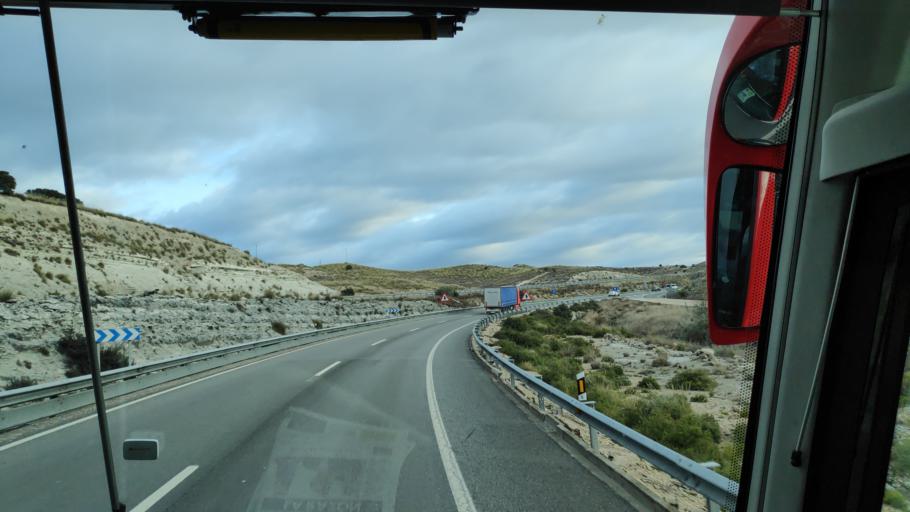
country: ES
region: Madrid
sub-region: Provincia de Madrid
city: Tielmes
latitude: 40.2075
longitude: -3.3161
